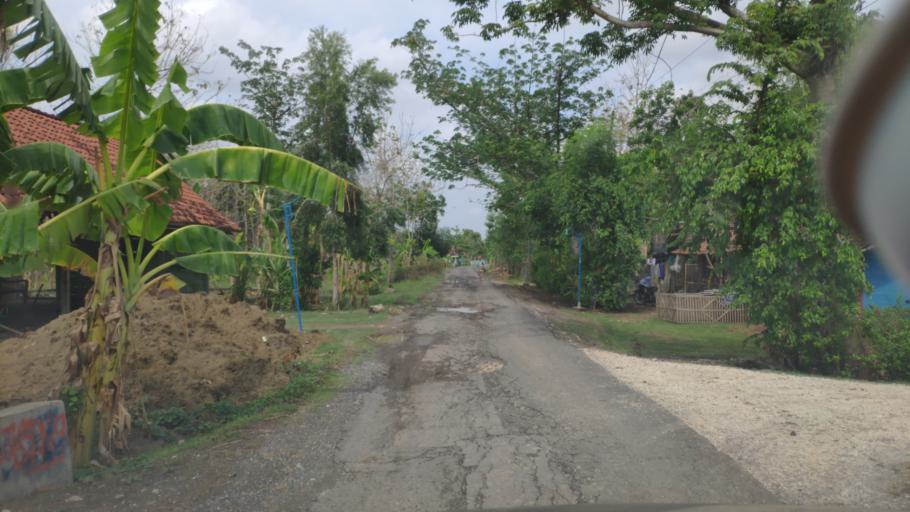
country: ID
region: Central Java
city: Ngablak
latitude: -7.0195
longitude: 111.3902
